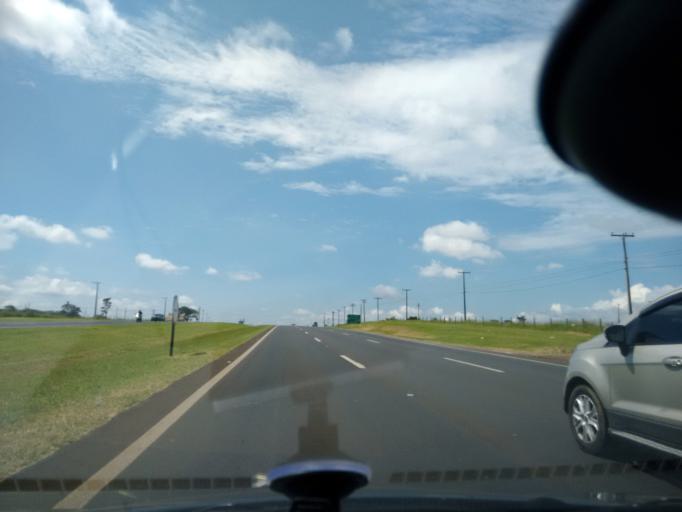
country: BR
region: Sao Paulo
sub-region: Sao Carlos
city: Sao Carlos
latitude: -21.9752
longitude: -47.9365
